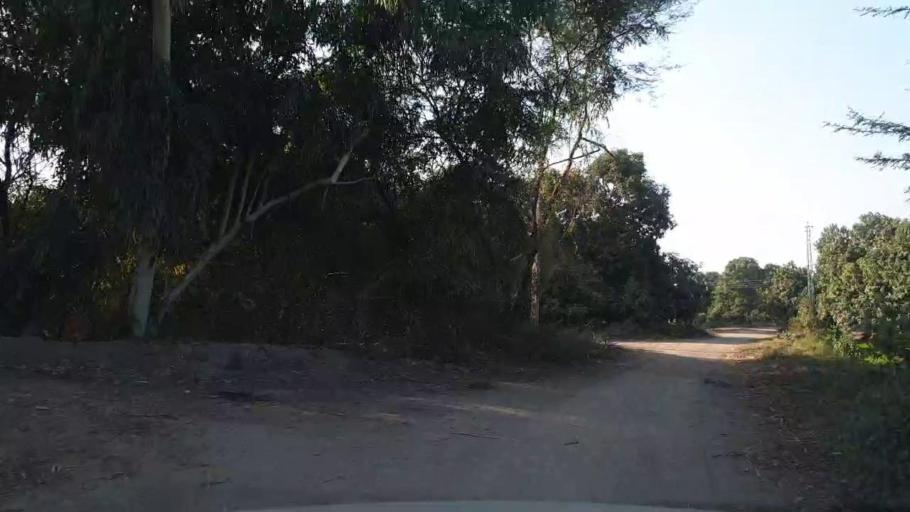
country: PK
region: Sindh
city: Tando Allahyar
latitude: 25.4869
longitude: 68.6416
